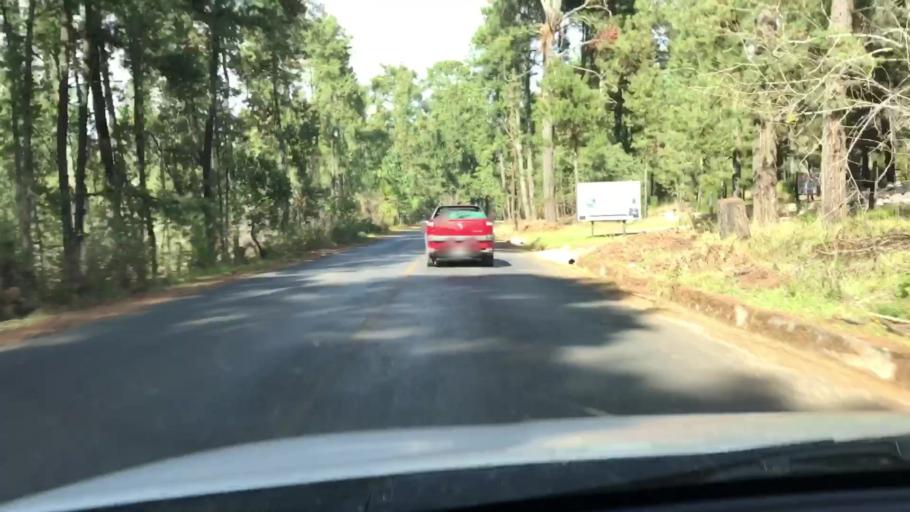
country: MX
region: Jalisco
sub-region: Amacueca
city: Tepec
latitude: 20.0861
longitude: -103.7157
